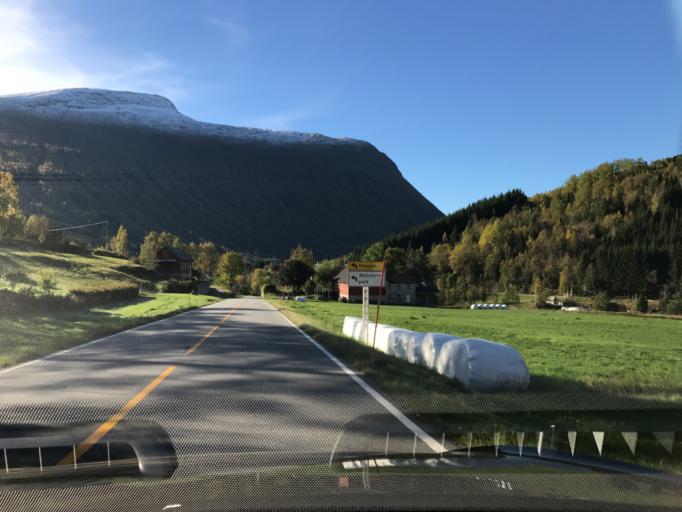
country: NO
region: More og Romsdal
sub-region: Norddal
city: Valldal
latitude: 62.3392
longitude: 7.3928
